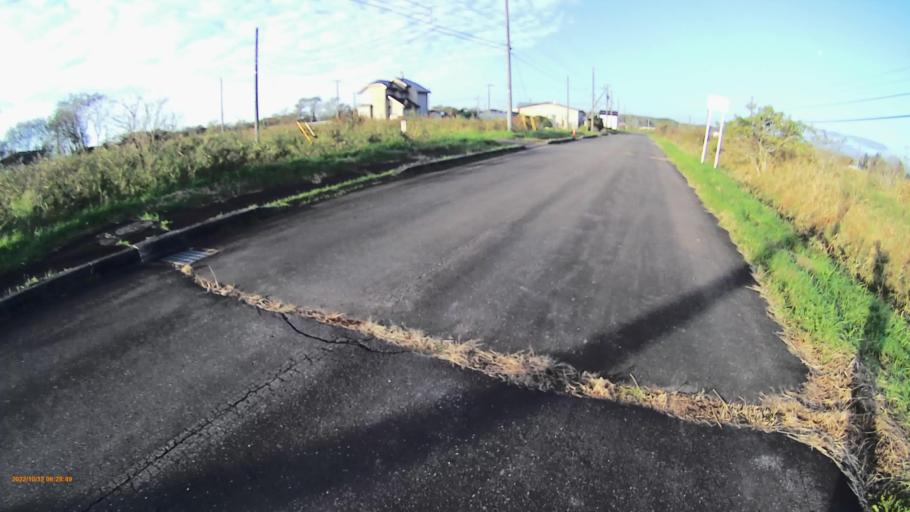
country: JP
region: Hokkaido
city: Kushiro
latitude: 42.8905
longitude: 143.9406
